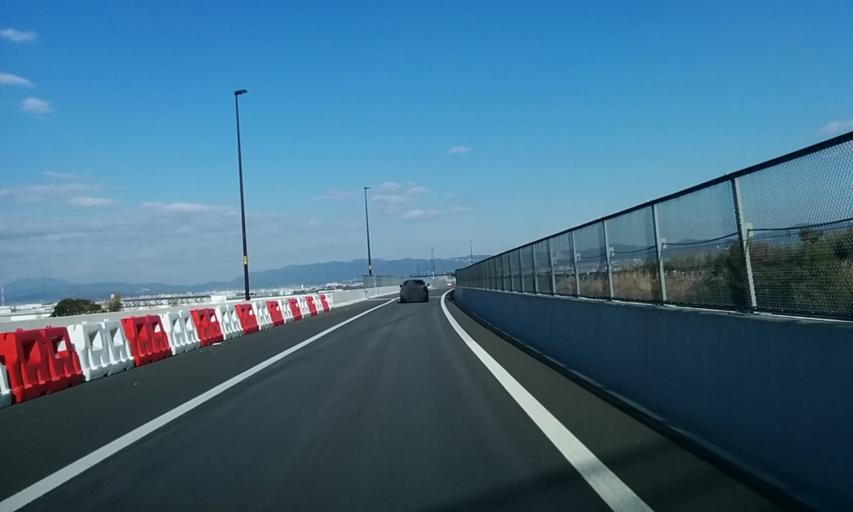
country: JP
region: Kyoto
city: Yawata
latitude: 34.8460
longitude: 135.7249
